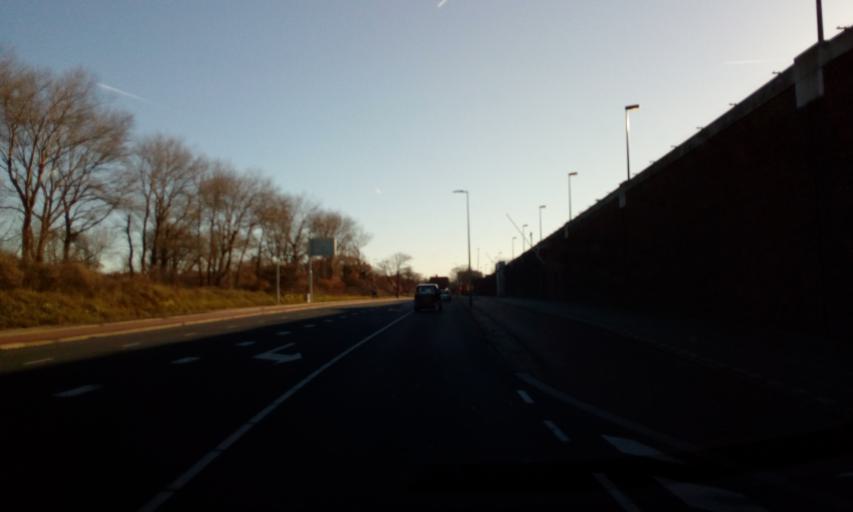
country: NL
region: South Holland
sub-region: Gemeente Den Haag
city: Scheveningen
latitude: 52.1118
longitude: 4.3002
